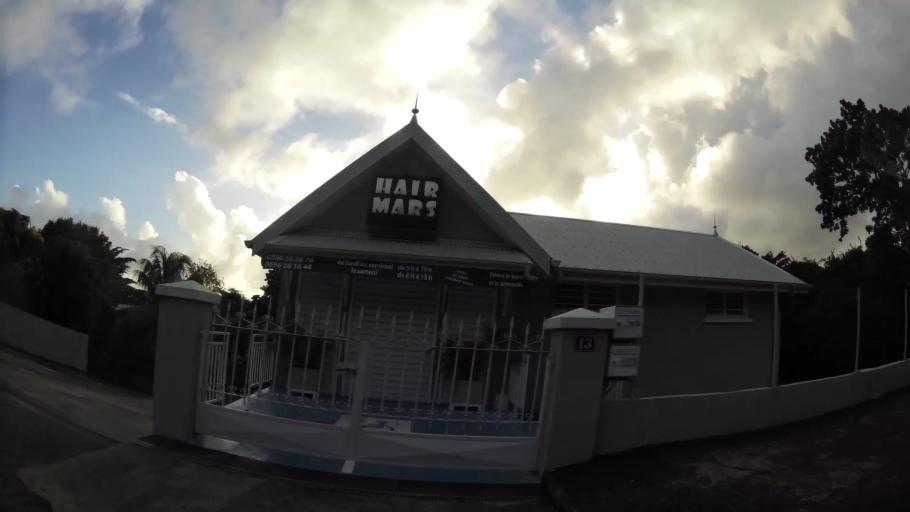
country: MQ
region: Martinique
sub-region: Martinique
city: Fort-de-France
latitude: 14.6137
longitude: -61.0811
